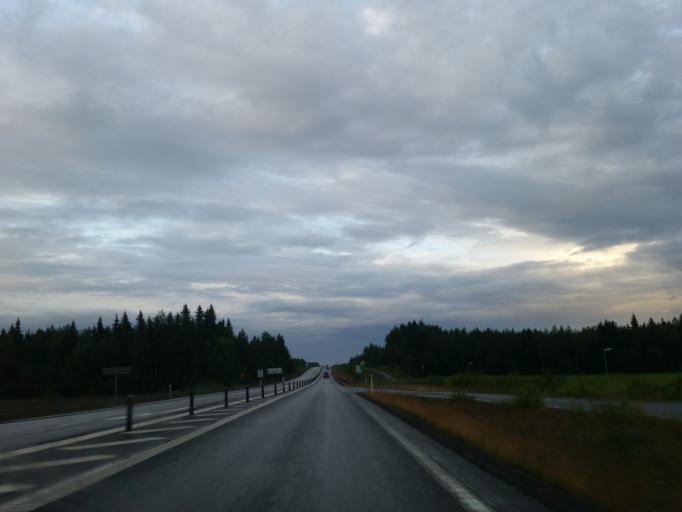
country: SE
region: Vaesterbotten
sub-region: Umea Kommun
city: Taftea
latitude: 63.8712
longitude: 20.4530
